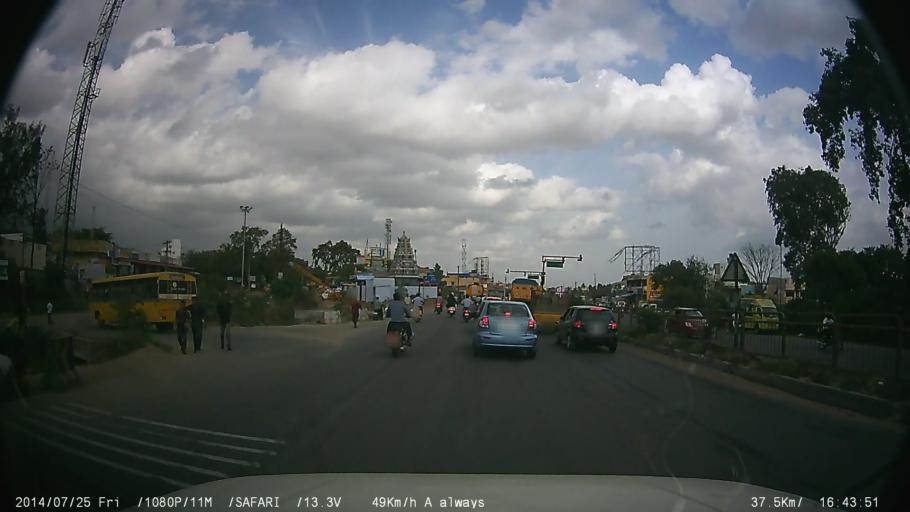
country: IN
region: Tamil Nadu
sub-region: Krishnagiri
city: Hosur
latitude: 12.7463
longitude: 77.8139
